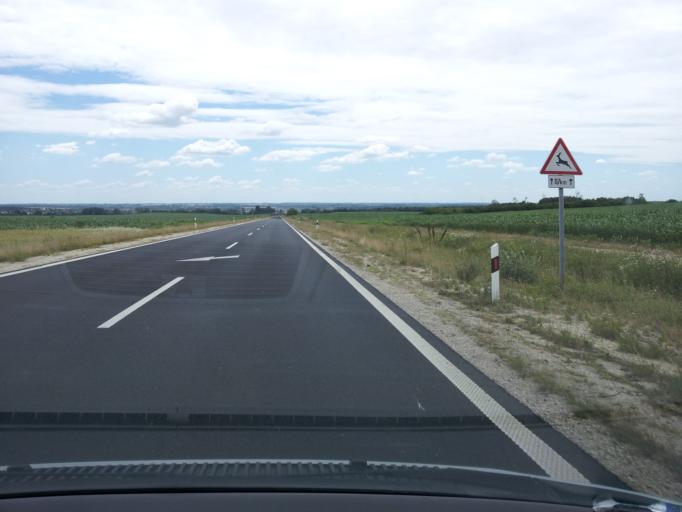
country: HU
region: Veszprem
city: Balatonkenese
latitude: 47.0348
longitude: 18.1652
